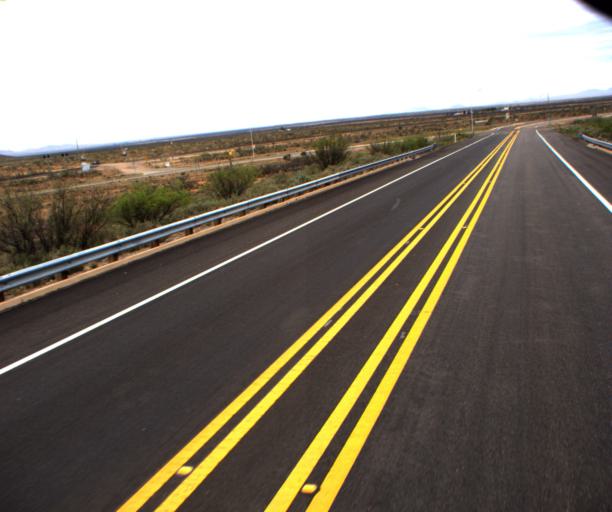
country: US
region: Arizona
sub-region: Cochise County
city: Willcox
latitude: 32.3063
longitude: -109.7968
